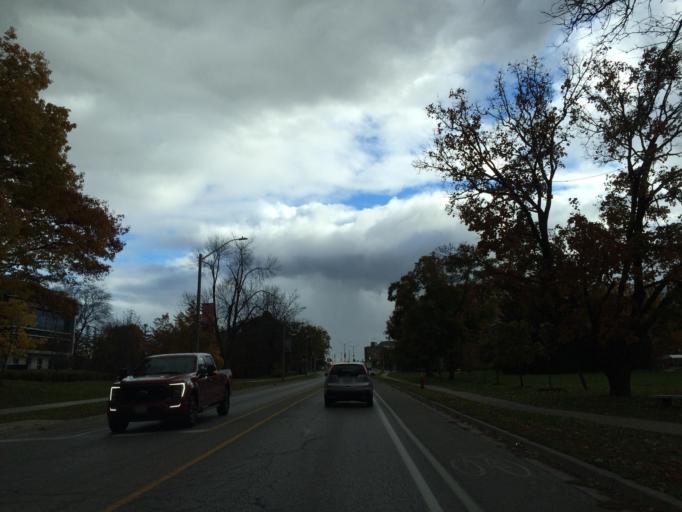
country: CA
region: Ontario
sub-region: Wellington County
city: Guelph
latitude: 43.5294
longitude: -80.2287
